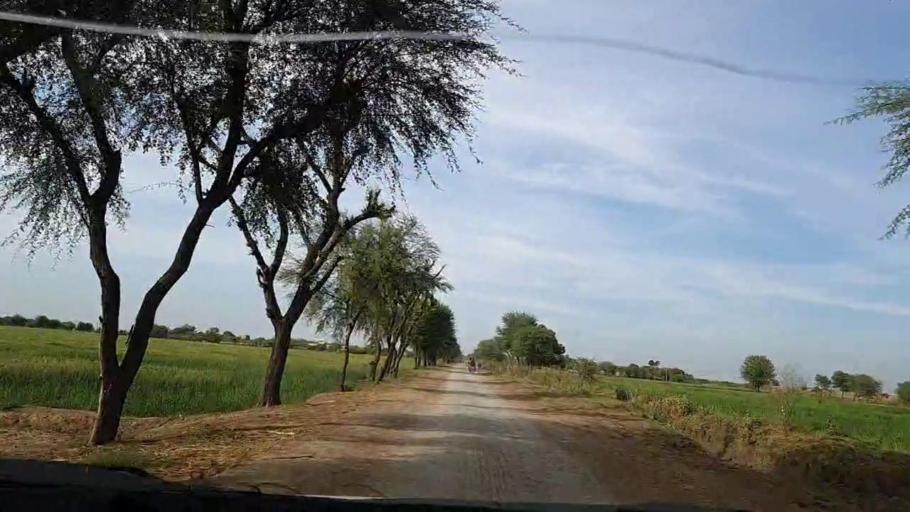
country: PK
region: Sindh
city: Dhoro Naro
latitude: 25.4449
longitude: 69.5124
